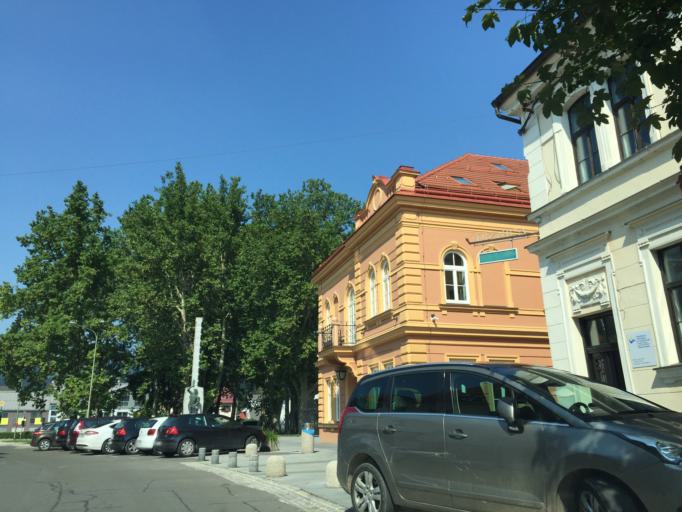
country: SI
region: Slovenj Gradec
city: Slovenj Gradec
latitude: 46.5102
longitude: 15.0801
